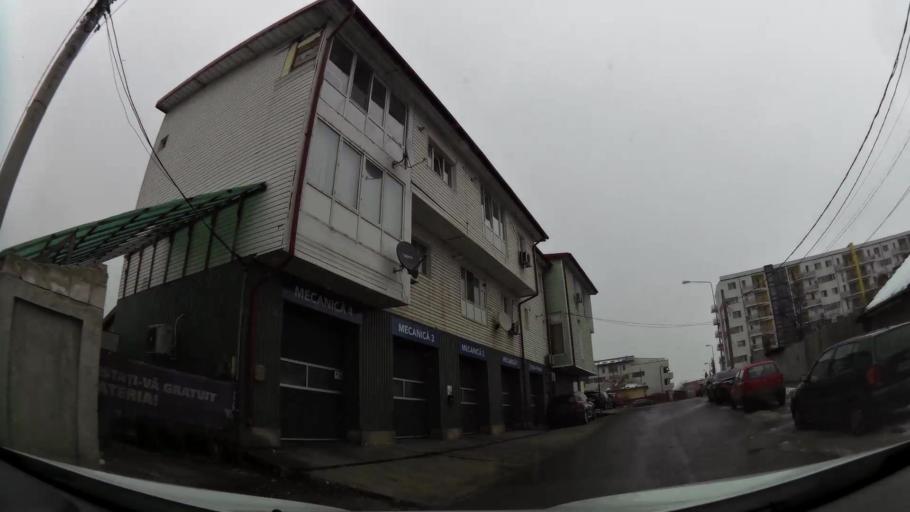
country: RO
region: Ilfov
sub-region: Comuna Popesti-Leordeni
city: Popesti-Leordeni
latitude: 44.4059
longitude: 26.1624
